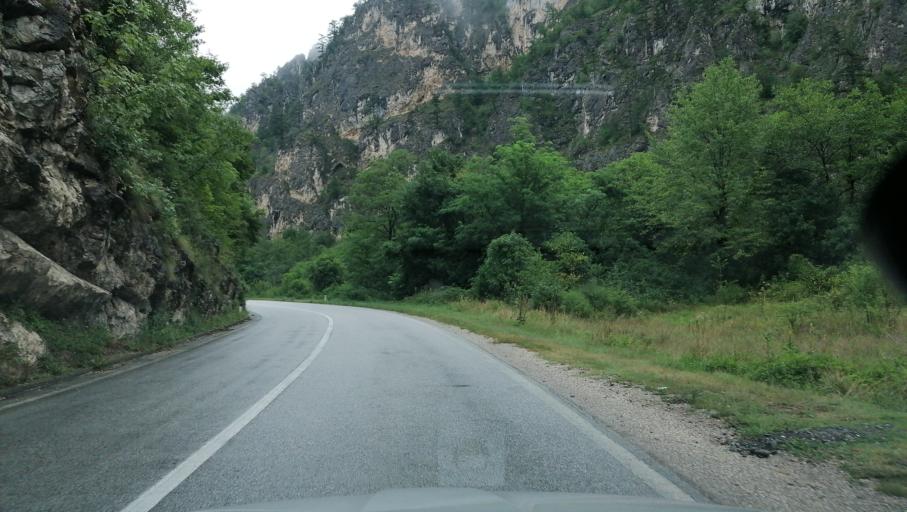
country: RS
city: Durici
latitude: 43.7521
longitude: 19.4003
